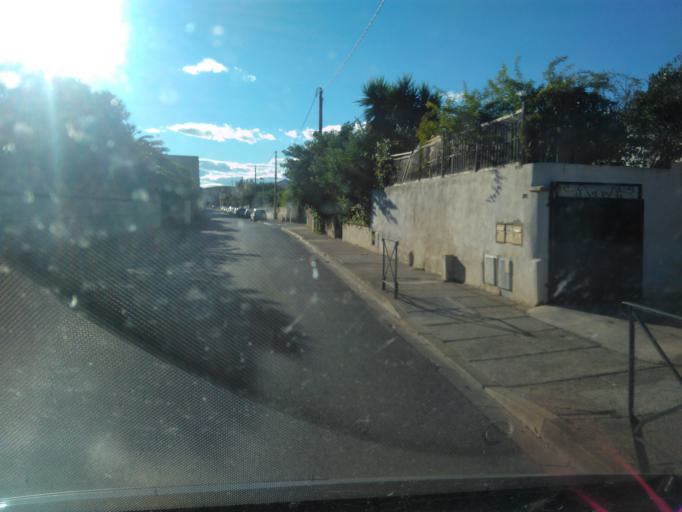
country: FR
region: Languedoc-Roussillon
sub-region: Departement de l'Herault
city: Lunel
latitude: 43.6745
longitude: 4.1422
